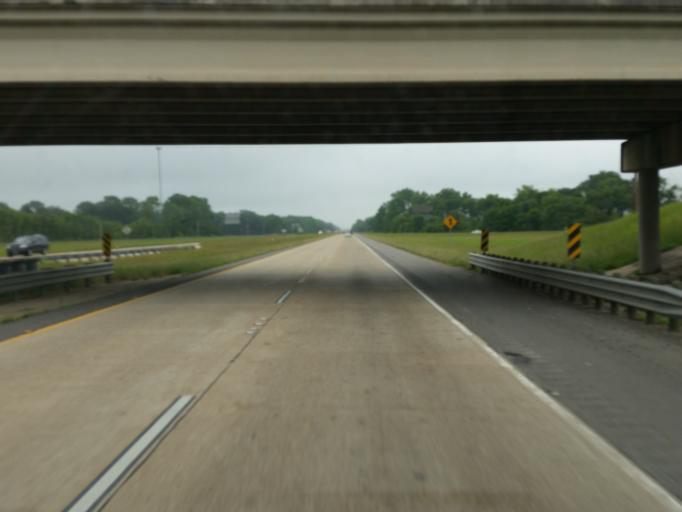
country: US
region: Louisiana
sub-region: Madison Parish
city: Tallulah
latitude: 32.3803
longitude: -91.1720
